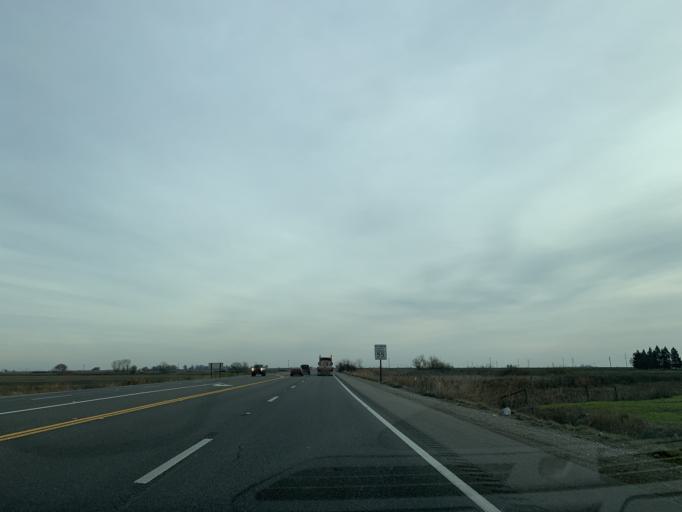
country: US
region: California
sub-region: Yuba County
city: Plumas Lake
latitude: 38.8845
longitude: -121.5698
